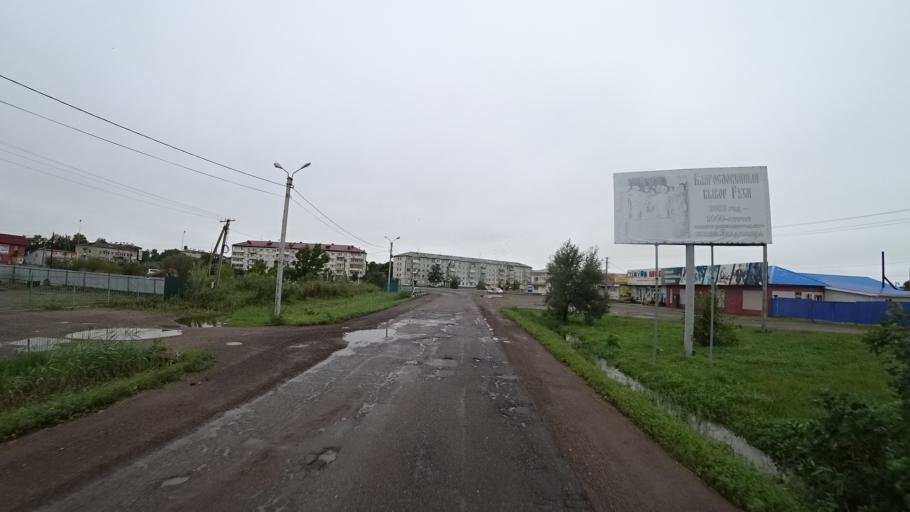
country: RU
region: Primorskiy
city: Monastyrishche
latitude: 44.2035
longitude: 132.4516
